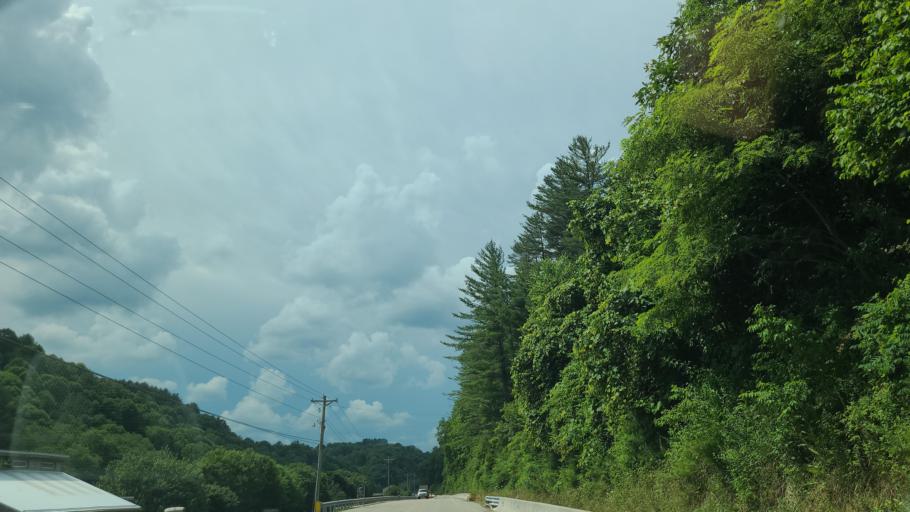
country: US
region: North Carolina
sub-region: Ashe County
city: Jefferson
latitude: 36.3873
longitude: -81.4022
